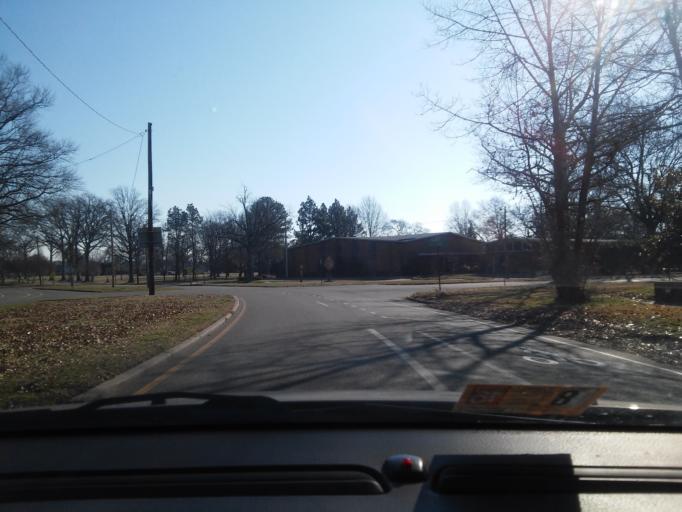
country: US
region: Virginia
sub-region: City of Richmond
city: Richmond
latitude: 37.5727
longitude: -77.4537
